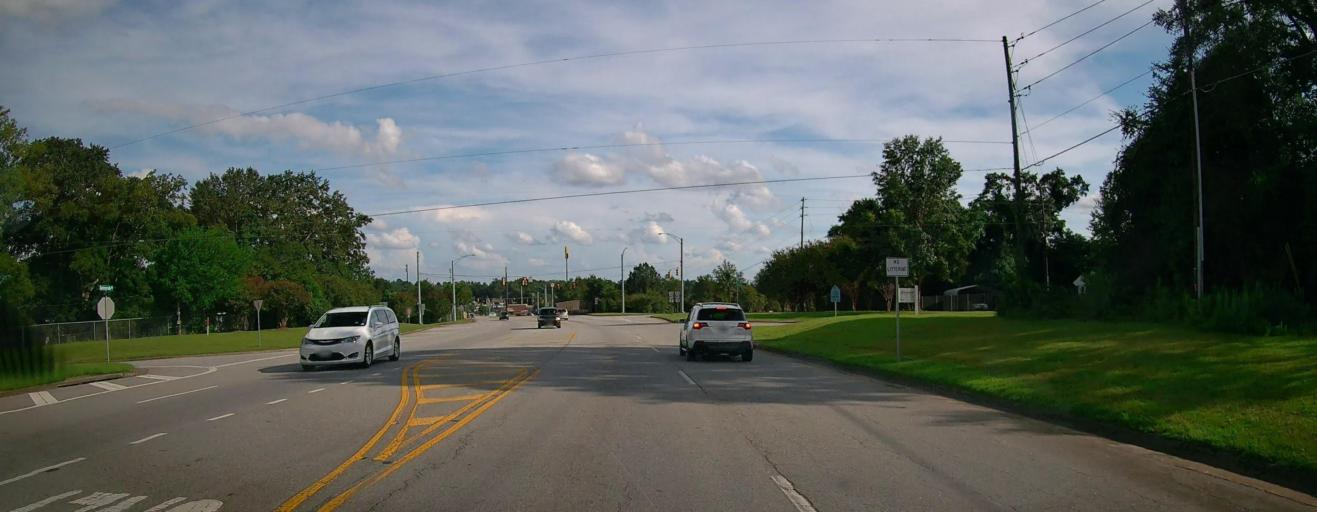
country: US
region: Alabama
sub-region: Russell County
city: Phenix City
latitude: 32.5012
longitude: -85.0187
